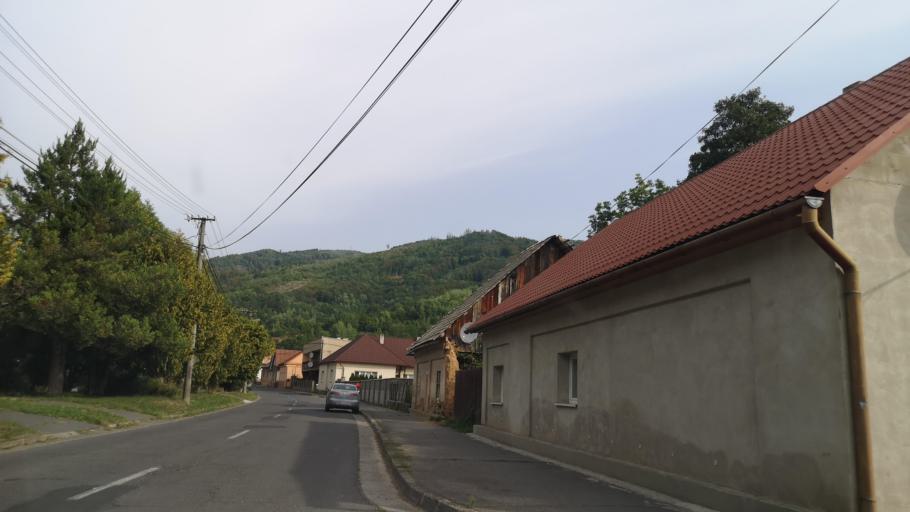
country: SK
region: Banskobystricky
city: Tisovec
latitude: 48.5748
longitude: 19.8397
